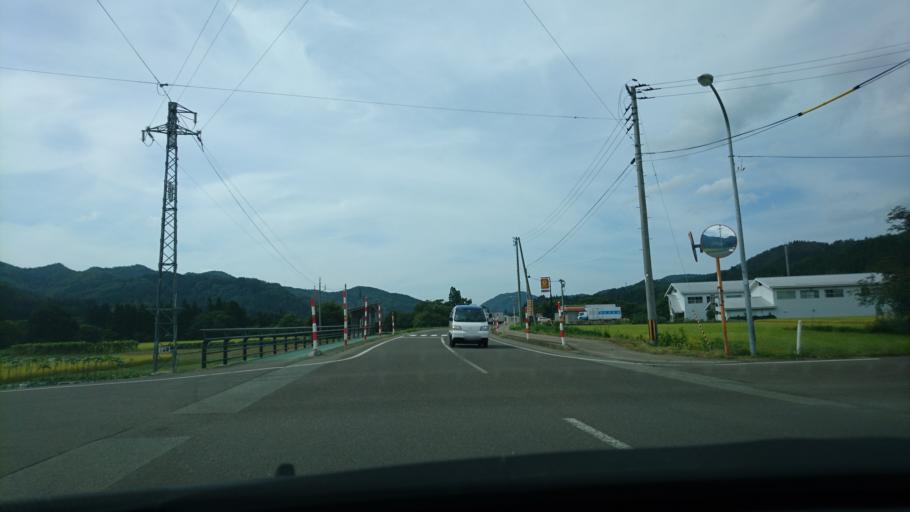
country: JP
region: Akita
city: Yuzawa
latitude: 39.1842
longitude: 140.6378
